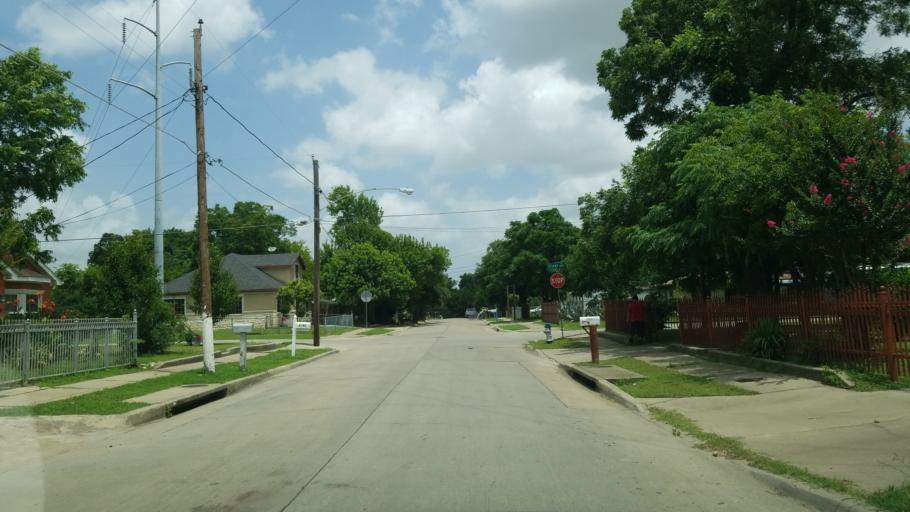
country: US
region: Texas
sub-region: Dallas County
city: Irving
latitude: 32.7914
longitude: -96.8992
